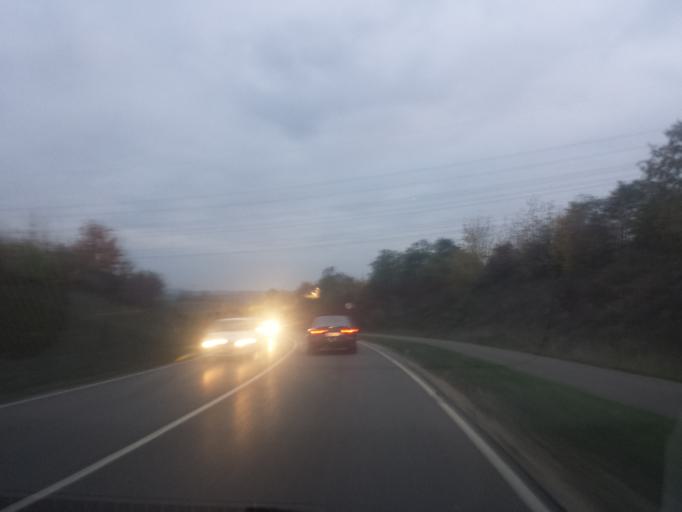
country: DE
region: Bavaria
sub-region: Upper Bavaria
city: Wettstetten
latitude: 48.8204
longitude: 11.4337
